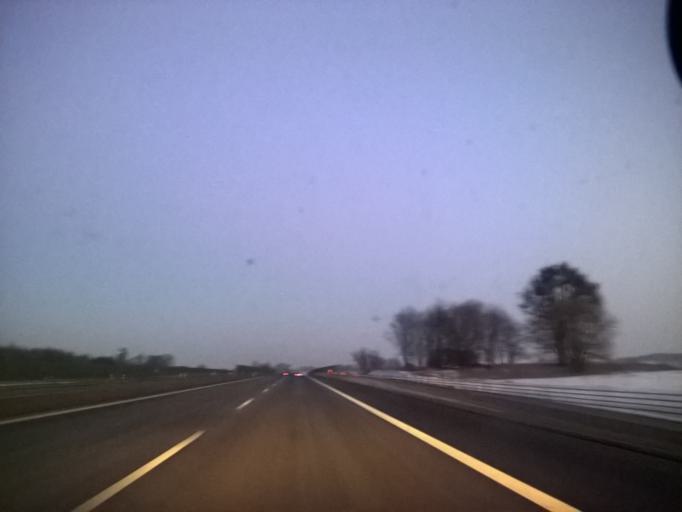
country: PL
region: Warmian-Masurian Voivodeship
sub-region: Powiat olsztynski
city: Biskupiec
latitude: 53.8416
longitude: 21.0064
